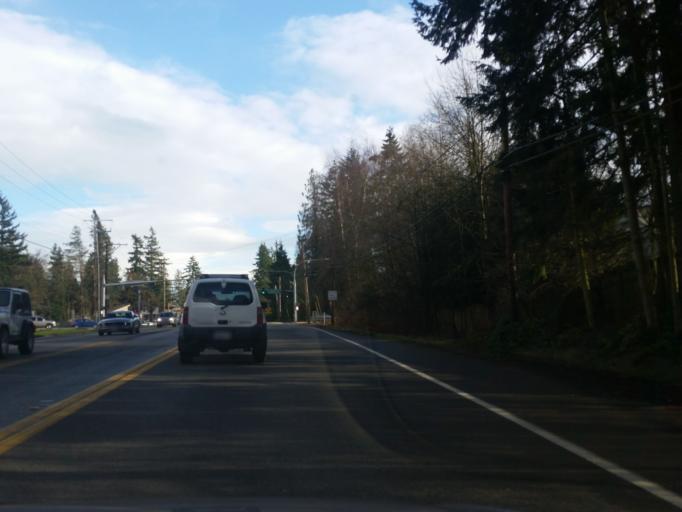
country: US
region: Washington
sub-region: Snohomish County
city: Martha Lake
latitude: 47.8247
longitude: -122.2399
